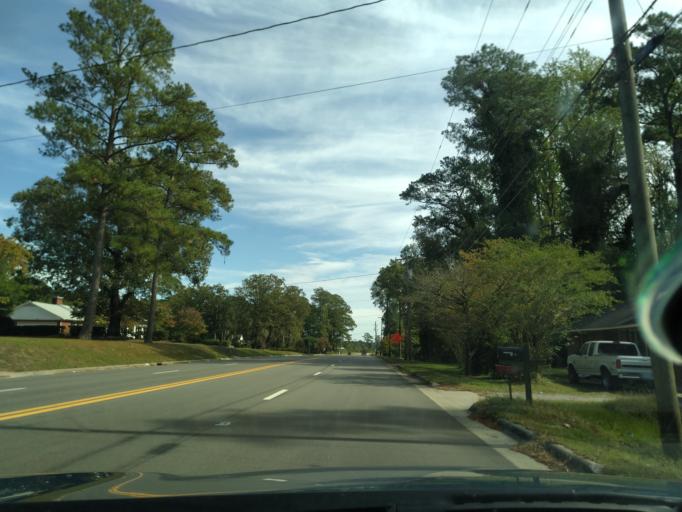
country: US
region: North Carolina
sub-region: Beaufort County
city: River Road
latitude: 35.5310
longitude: -77.0184
